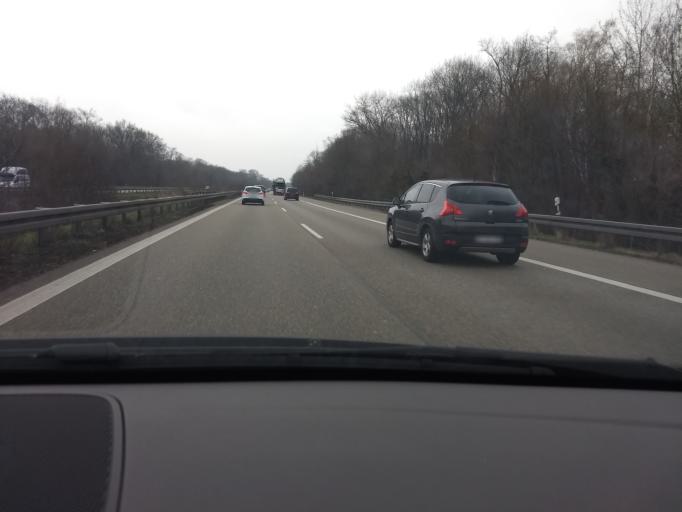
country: DE
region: Baden-Wuerttemberg
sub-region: Freiburg Region
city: Umkirch
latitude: 48.0098
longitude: 7.7653
